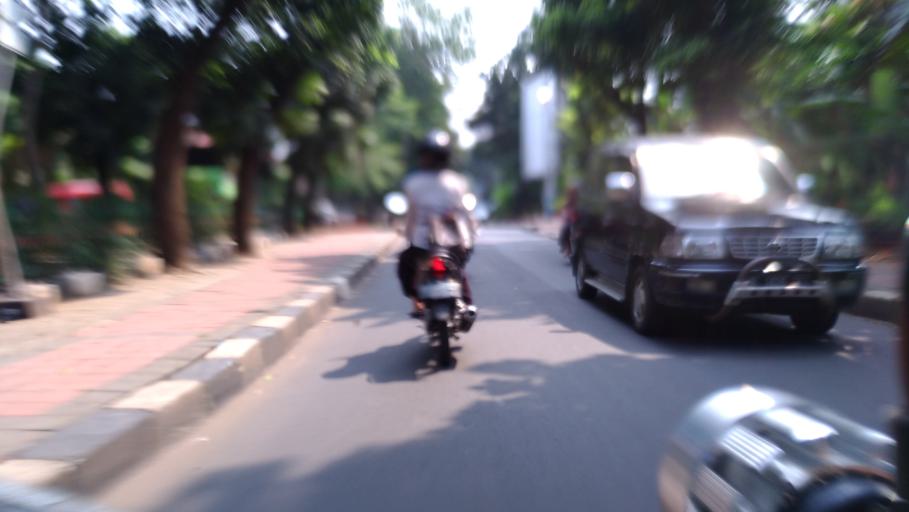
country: ID
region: West Java
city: Cileungsir
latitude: -6.3522
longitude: 106.8882
